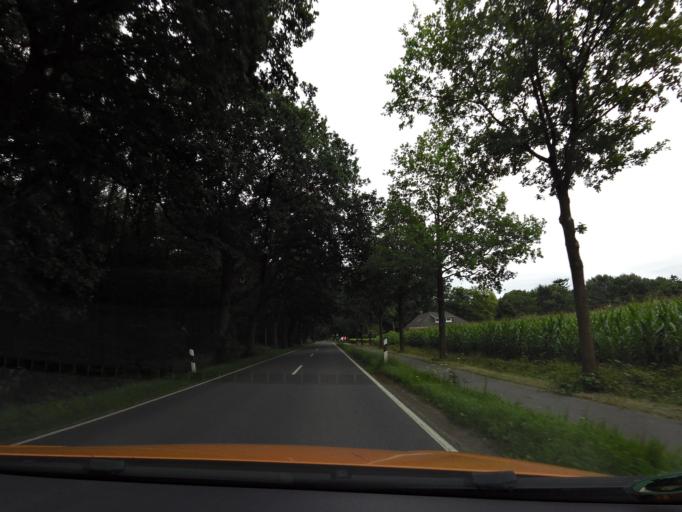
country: DE
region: Lower Saxony
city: Wiefelstede
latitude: 53.2053
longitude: 8.1159
